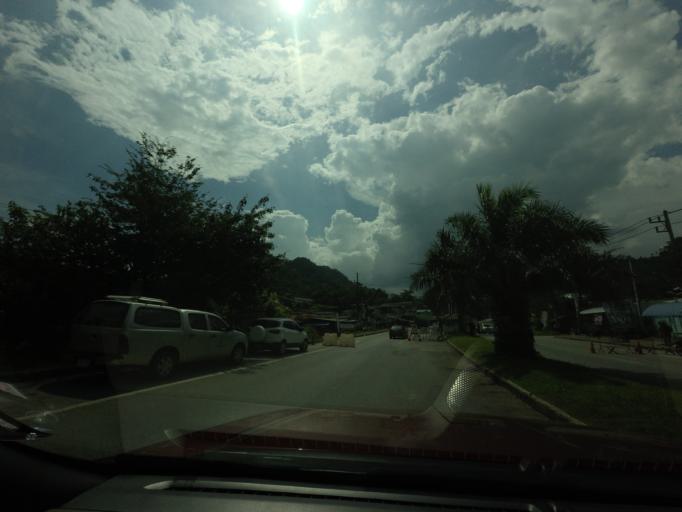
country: TH
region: Yala
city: Than To
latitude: 6.1652
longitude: 101.1816
